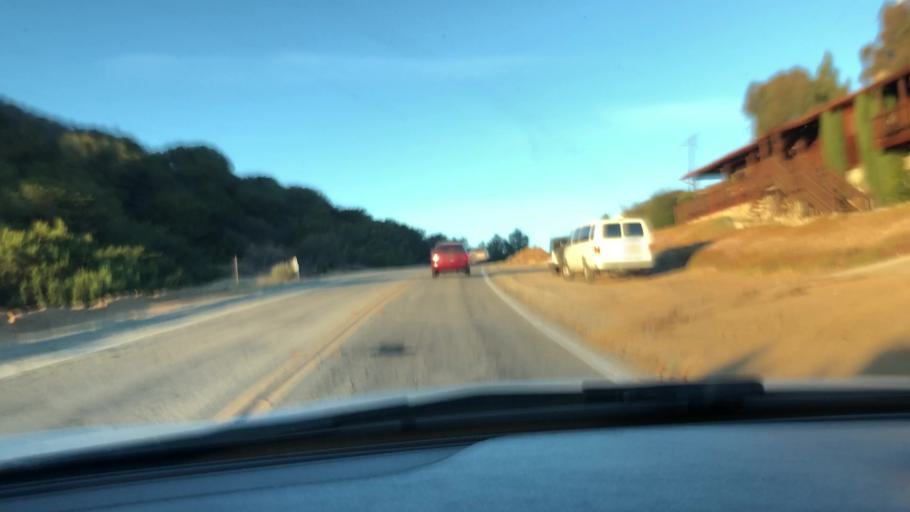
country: US
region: California
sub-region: Los Angeles County
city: Green Valley
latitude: 34.6589
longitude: -118.3530
